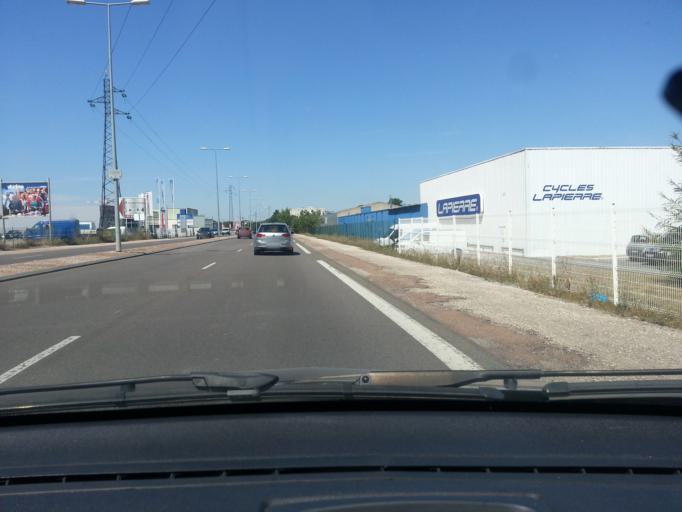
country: FR
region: Bourgogne
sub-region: Departement de la Cote-d'Or
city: Chenove
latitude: 47.2976
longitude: 5.0234
